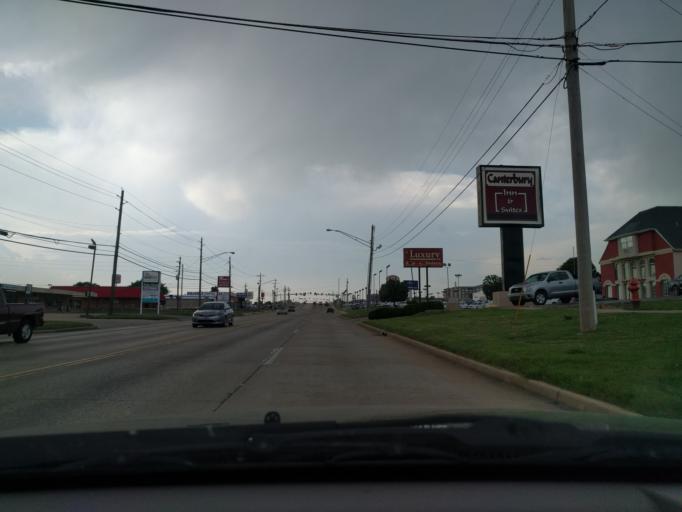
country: US
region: Oklahoma
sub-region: Tulsa County
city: Broken Arrow
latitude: 36.0673
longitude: -95.7974
